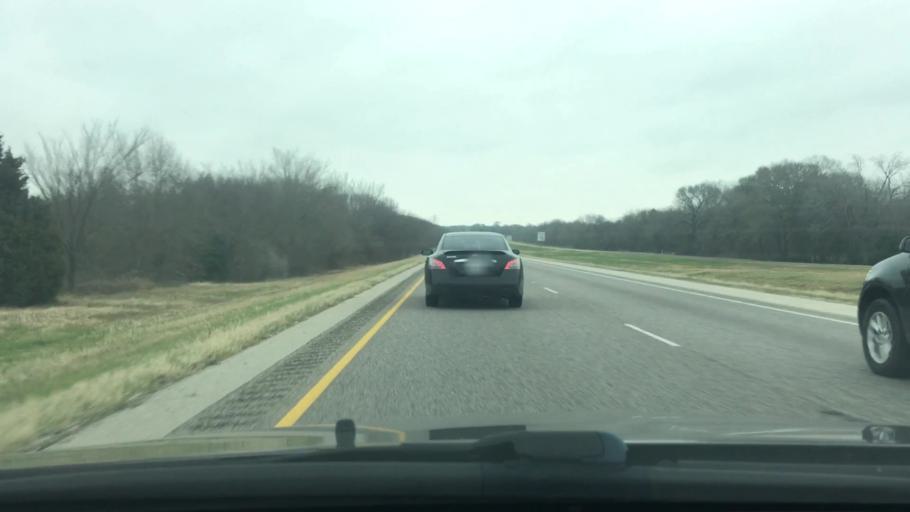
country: US
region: Texas
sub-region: Freestone County
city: Fairfield
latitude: 31.8016
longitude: -96.2598
